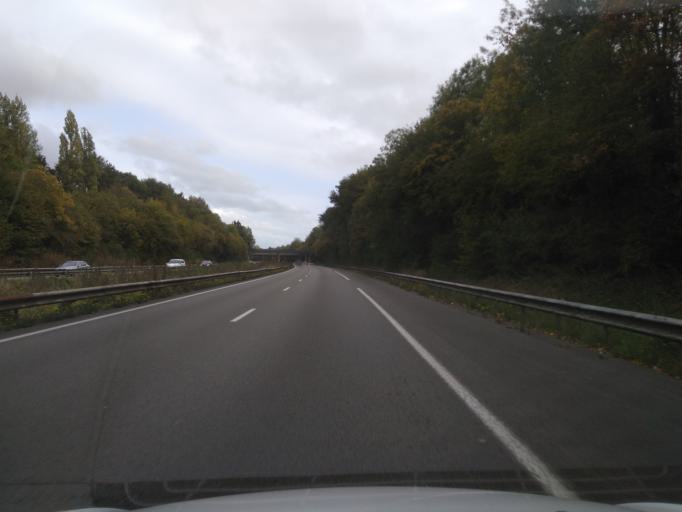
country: FR
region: Nord-Pas-de-Calais
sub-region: Departement du Nord
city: Saultain
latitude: 50.3389
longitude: 3.5634
